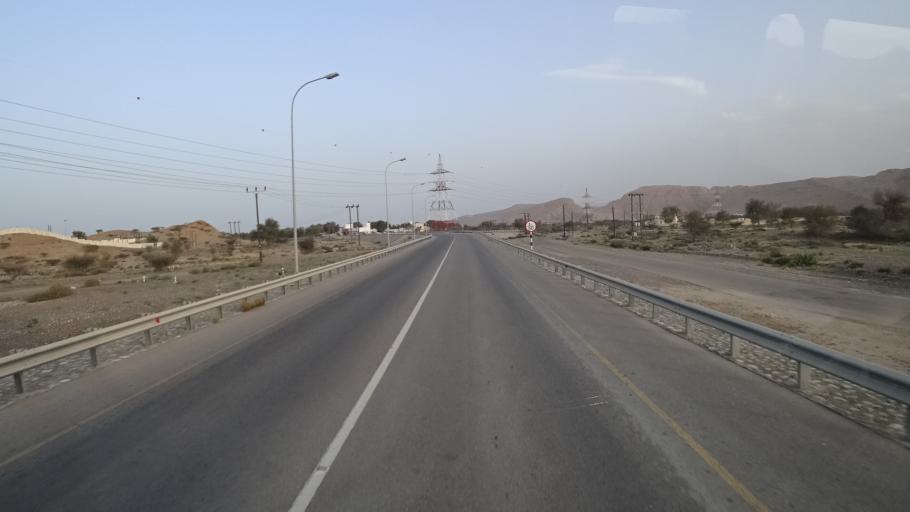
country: OM
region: Muhafazat Masqat
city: Muscat
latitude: 23.2066
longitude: 58.9493
